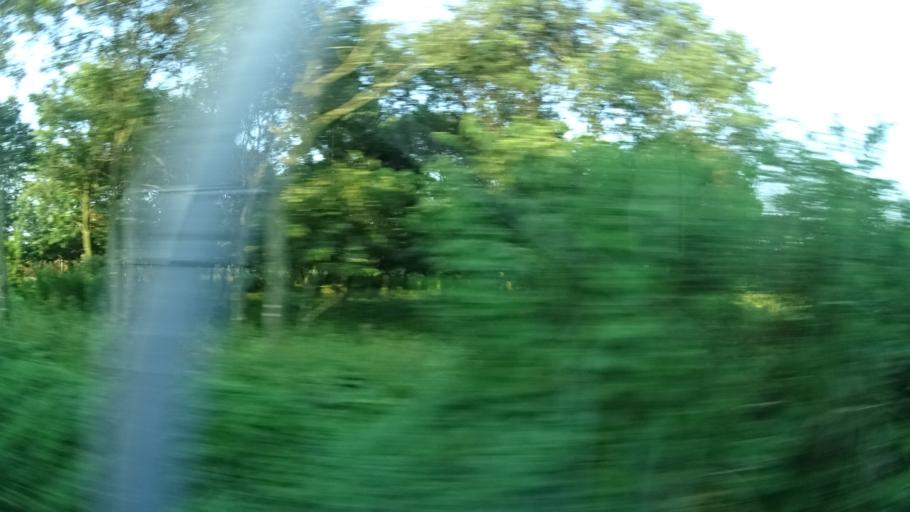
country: JP
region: Ibaraki
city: Tomobe
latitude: 36.2768
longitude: 140.2796
